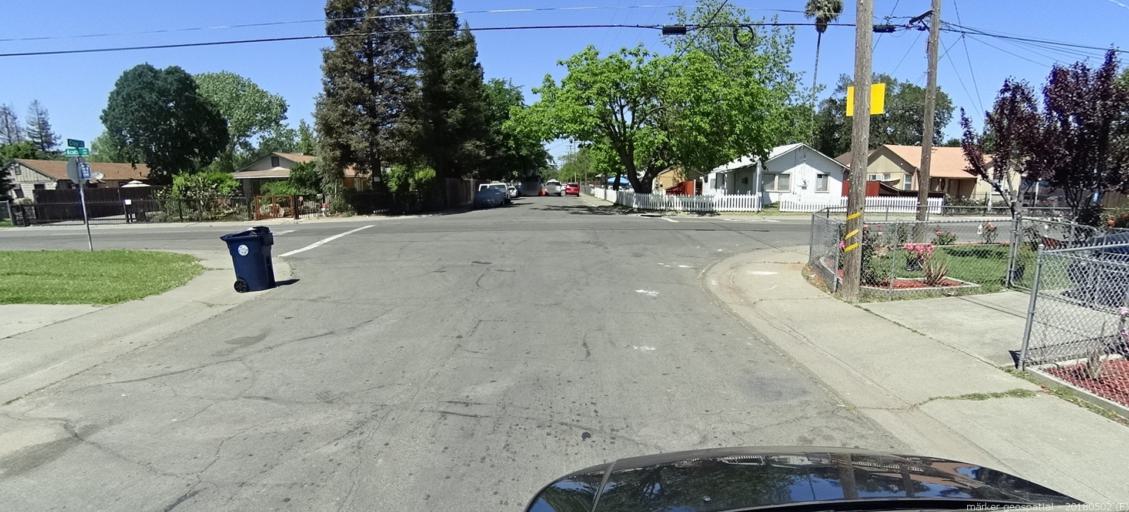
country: US
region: California
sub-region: Sacramento County
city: Arden-Arcade
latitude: 38.6218
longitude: -121.4393
